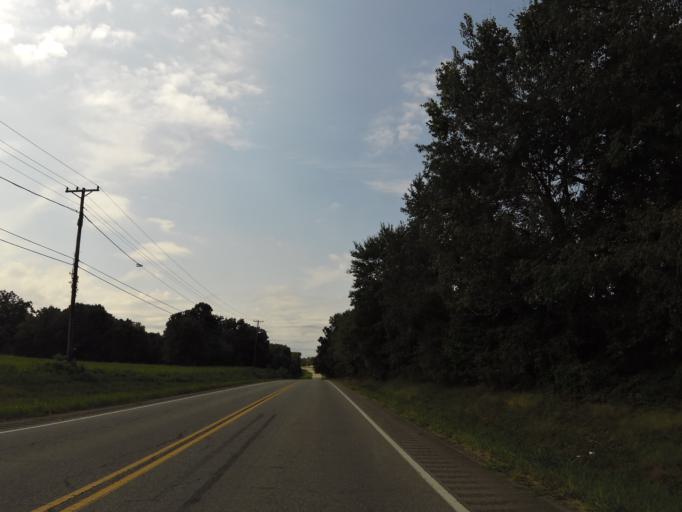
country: US
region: Tennessee
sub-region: Humphreys County
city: Waverly
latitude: 35.8719
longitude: -87.8065
